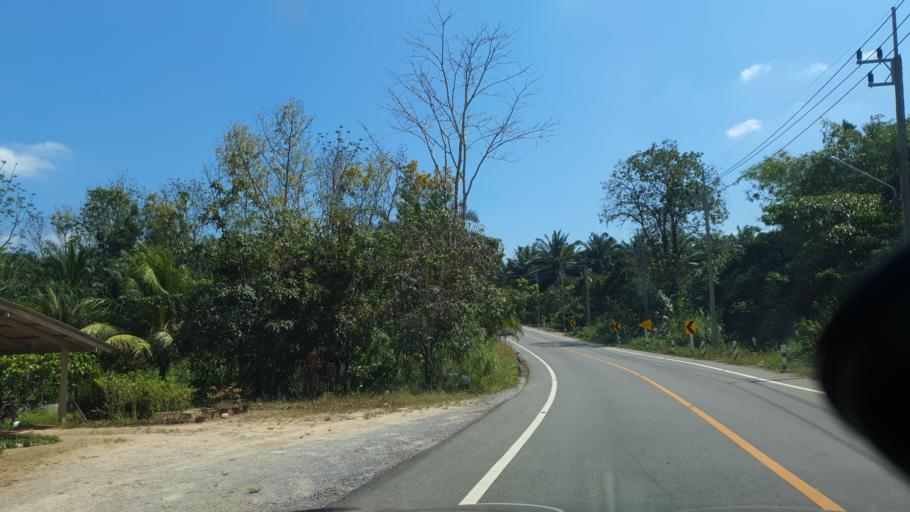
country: TH
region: Krabi
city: Khlong Thom
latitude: 7.9293
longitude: 99.2313
